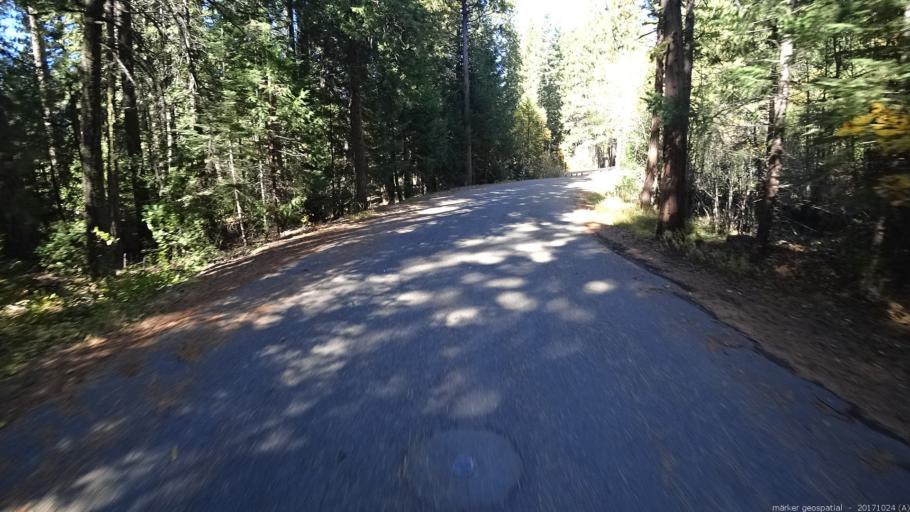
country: US
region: California
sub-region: Shasta County
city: Shingletown
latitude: 40.4999
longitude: -121.6595
